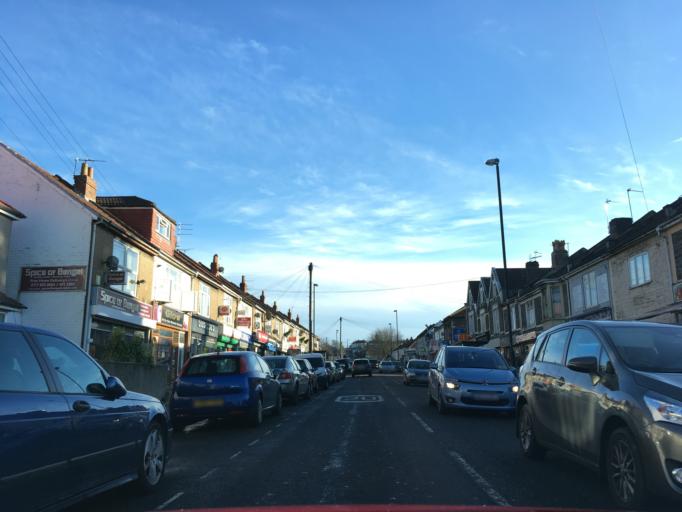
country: GB
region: England
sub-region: South Gloucestershire
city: Mangotsfield
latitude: 51.4727
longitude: -2.5257
